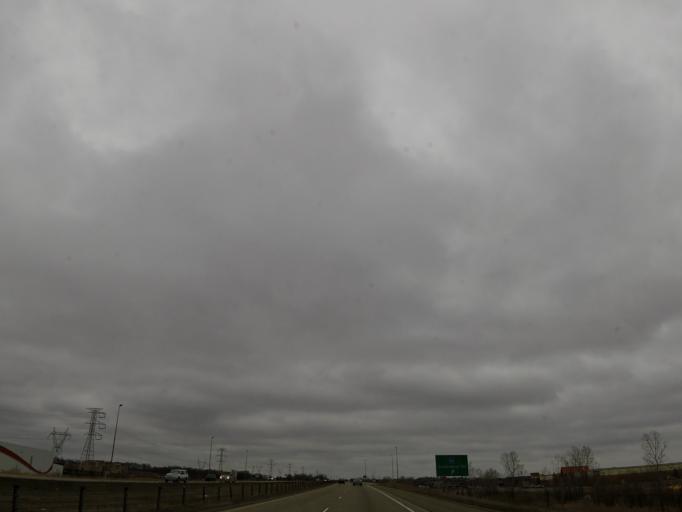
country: US
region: Minnesota
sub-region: Scott County
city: Shakopee
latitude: 44.7832
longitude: -93.4615
